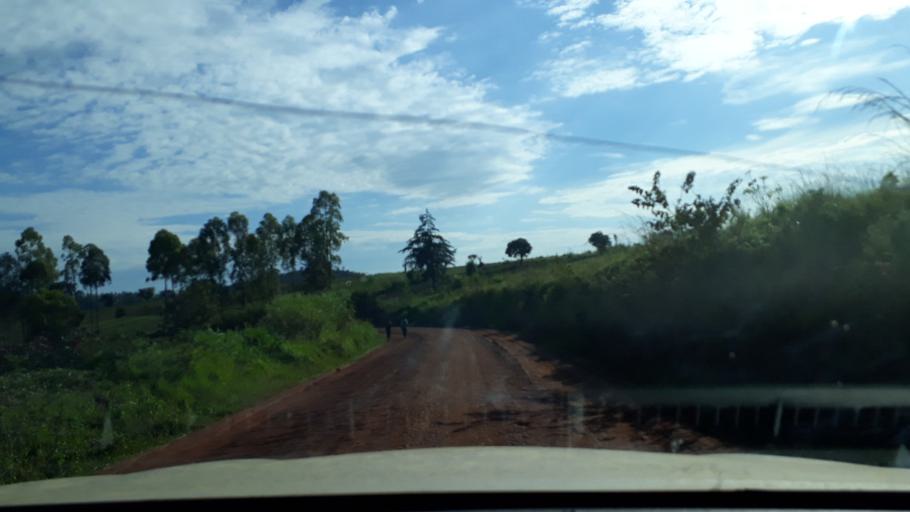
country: UG
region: Northern Region
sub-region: Zombo District
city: Paidha
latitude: 2.2695
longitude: 30.9564
